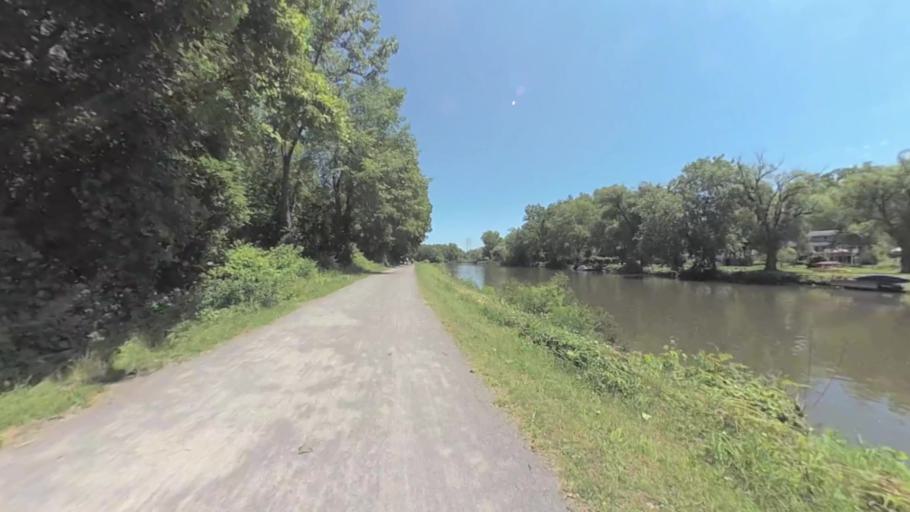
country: US
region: New York
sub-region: Monroe County
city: Fairport
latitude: 43.0855
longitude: -77.4583
